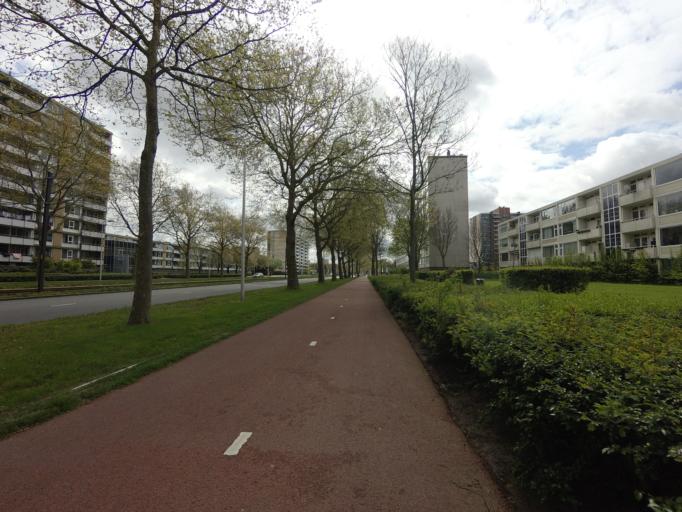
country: NL
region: Utrecht
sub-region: Gemeente Utrecht
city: Utrecht
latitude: 52.0773
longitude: 5.0939
